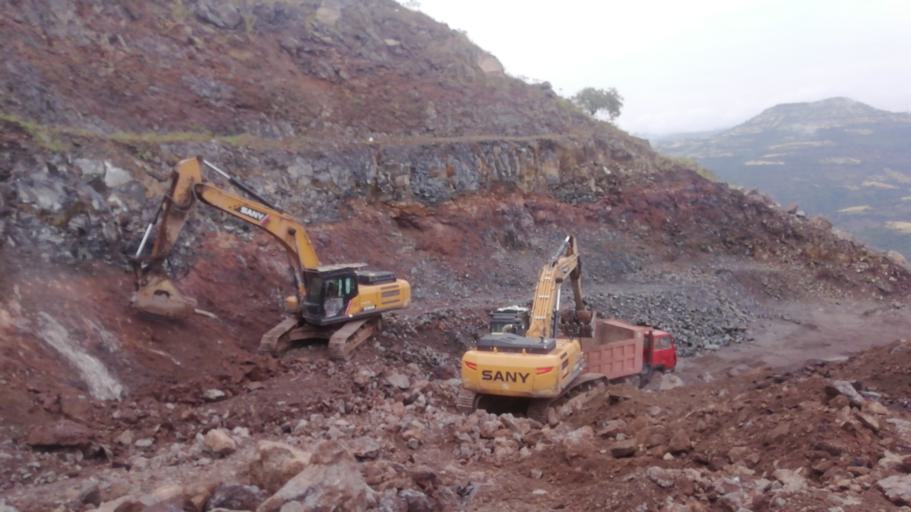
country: ET
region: Amhara
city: Addiet Canna
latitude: 11.2280
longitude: 37.8857
